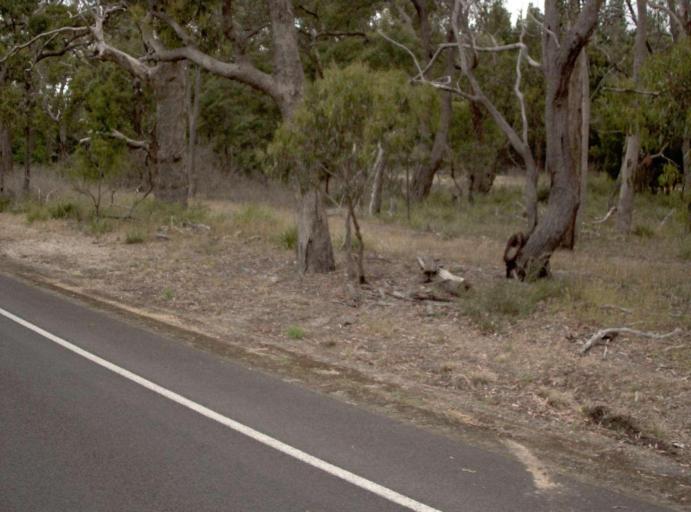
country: AU
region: Victoria
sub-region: Wellington
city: Sale
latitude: -38.2388
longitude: 147.0547
